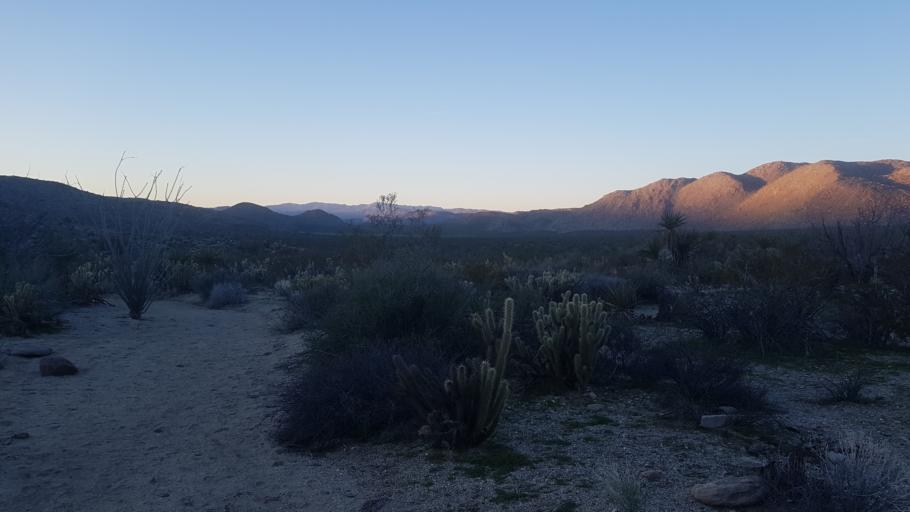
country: US
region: California
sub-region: San Diego County
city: Julian
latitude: 33.0085
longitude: -116.3776
